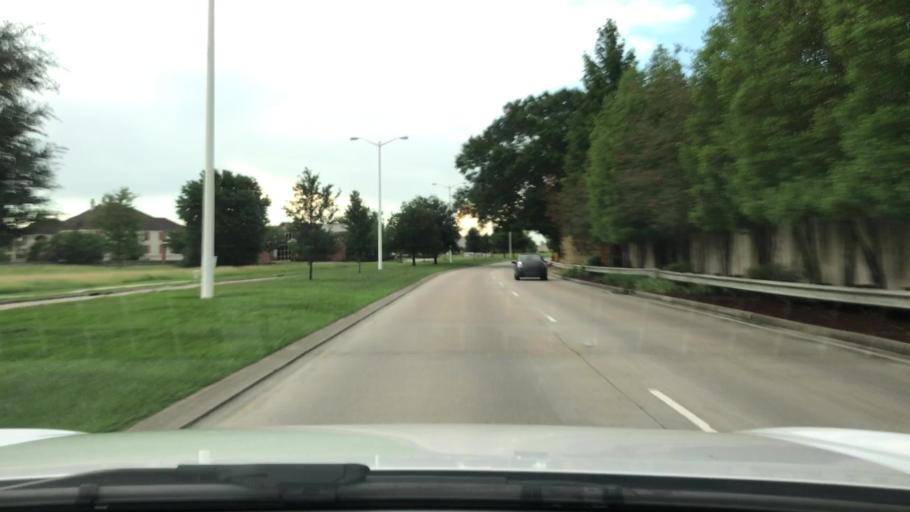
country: US
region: Louisiana
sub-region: East Baton Rouge Parish
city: Westminster
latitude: 30.4264
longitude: -91.1207
